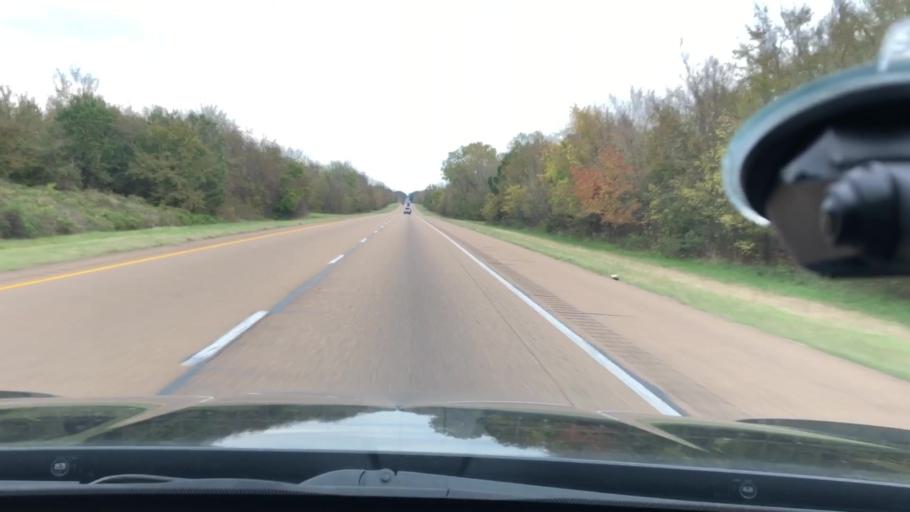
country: US
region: Arkansas
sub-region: Hempstead County
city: Hope
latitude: 33.7495
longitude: -93.5066
